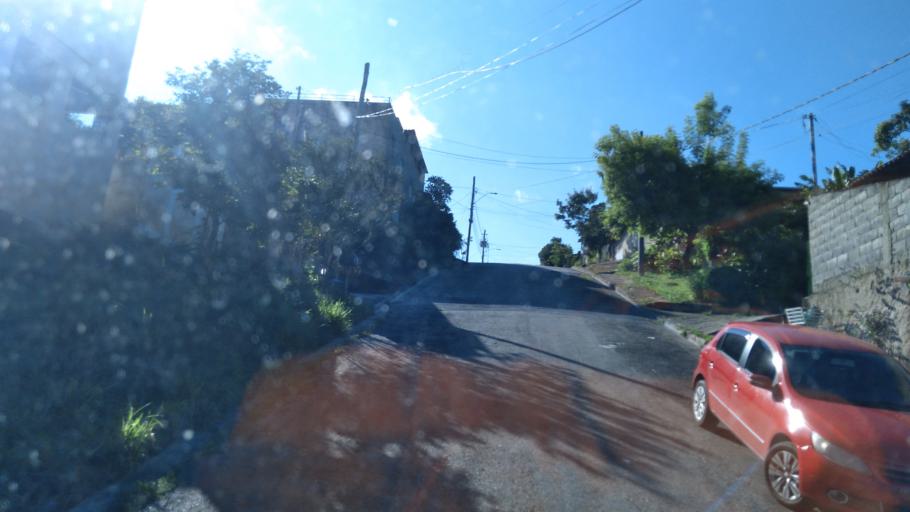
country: BR
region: Minas Gerais
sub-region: Santa Luzia
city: Santa Luzia
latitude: -19.8280
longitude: -43.9018
